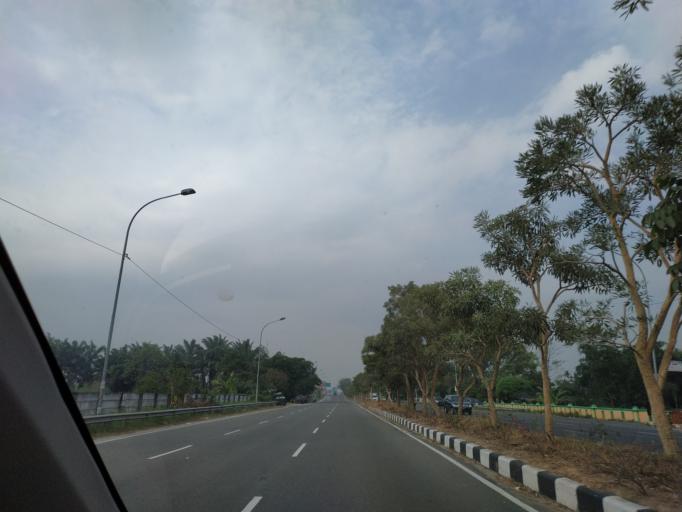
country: ID
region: North Sumatra
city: Percut
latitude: 3.6048
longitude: 98.8488
